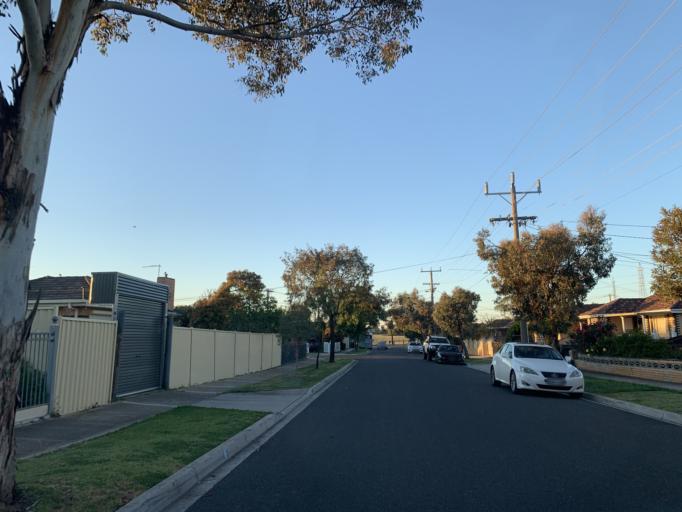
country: AU
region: Victoria
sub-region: Brimbank
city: St Albans
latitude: -37.7484
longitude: 144.8120
